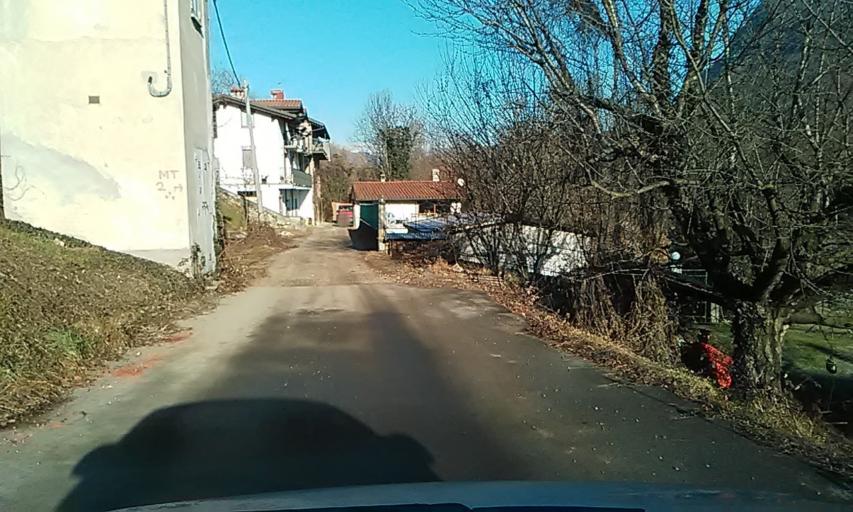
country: IT
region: Piedmont
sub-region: Provincia di Vercelli
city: Serravalle Sesia
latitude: 45.6896
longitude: 8.3095
